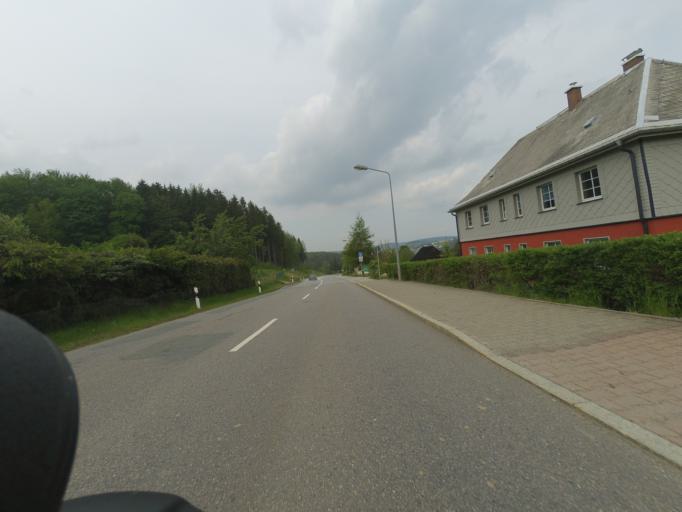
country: DE
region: Saxony
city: Zoblitz
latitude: 50.6589
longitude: 13.2214
